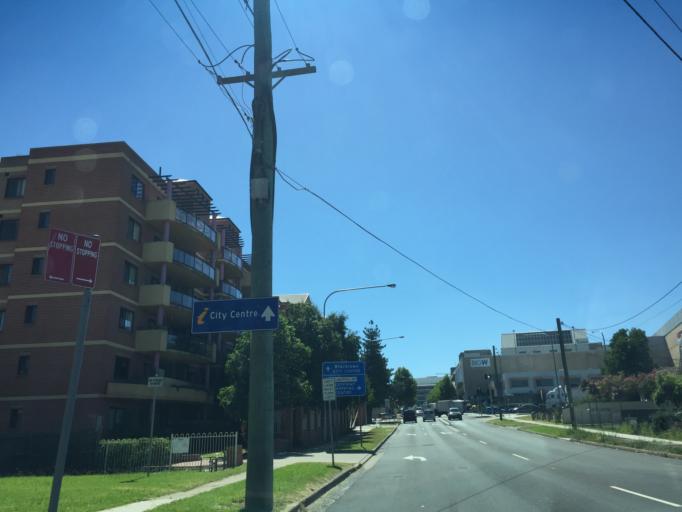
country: AU
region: New South Wales
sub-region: Blacktown
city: Blacktown
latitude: -33.7688
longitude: 150.9030
